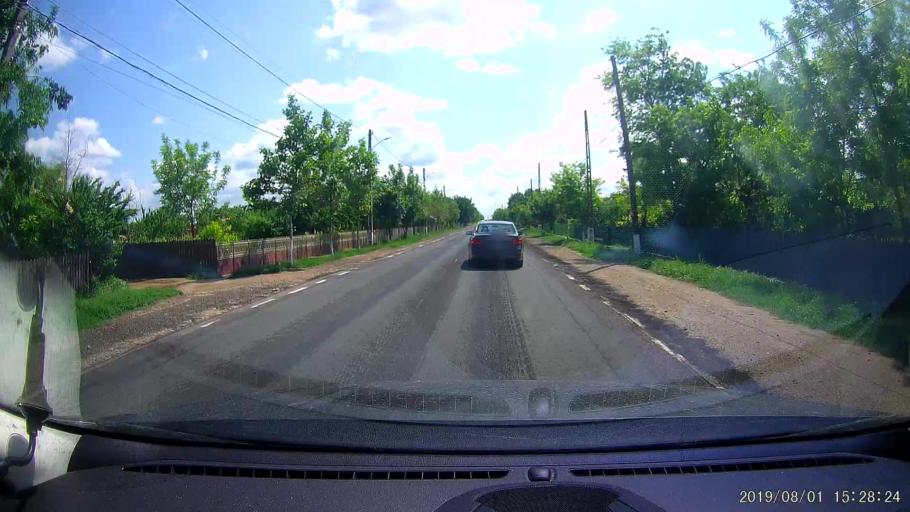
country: RO
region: Braila
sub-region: Comuna Viziru
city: Viziru
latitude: 44.9940
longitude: 27.7098
